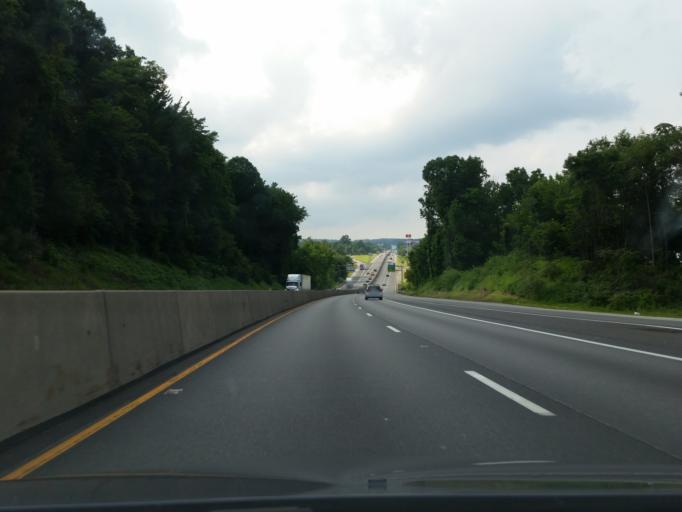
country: US
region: Pennsylvania
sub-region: York County
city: Valley Green
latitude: 40.1479
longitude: -76.8171
